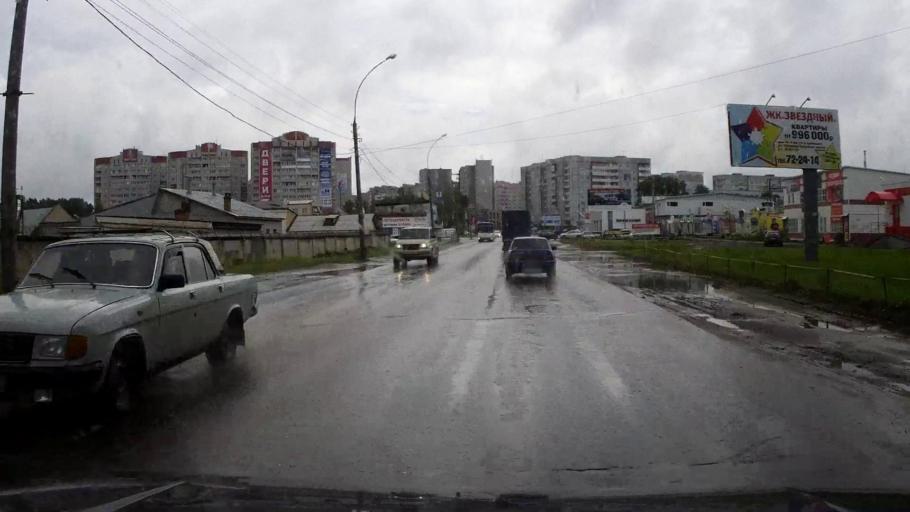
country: RU
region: Vologda
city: Vologda
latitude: 59.2049
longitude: 39.8653
